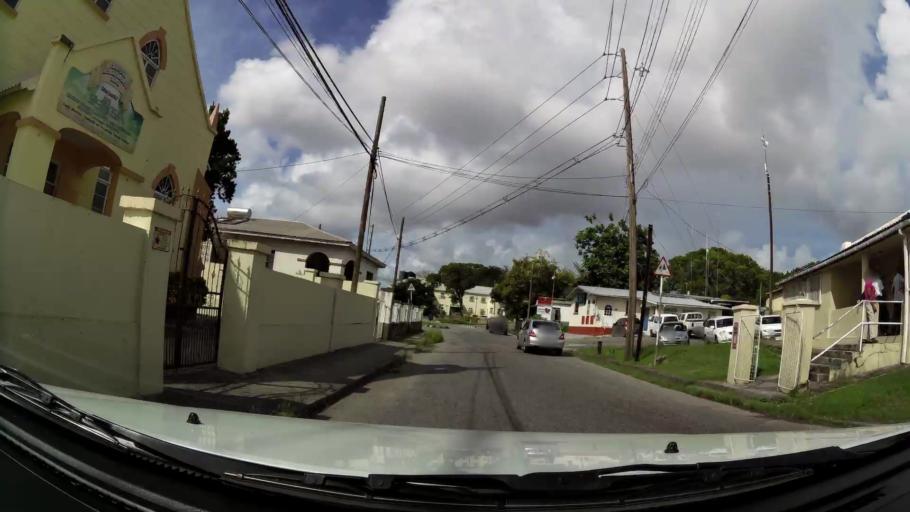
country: BB
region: Saint Michael
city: Bridgetown
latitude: 13.1045
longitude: -59.6017
